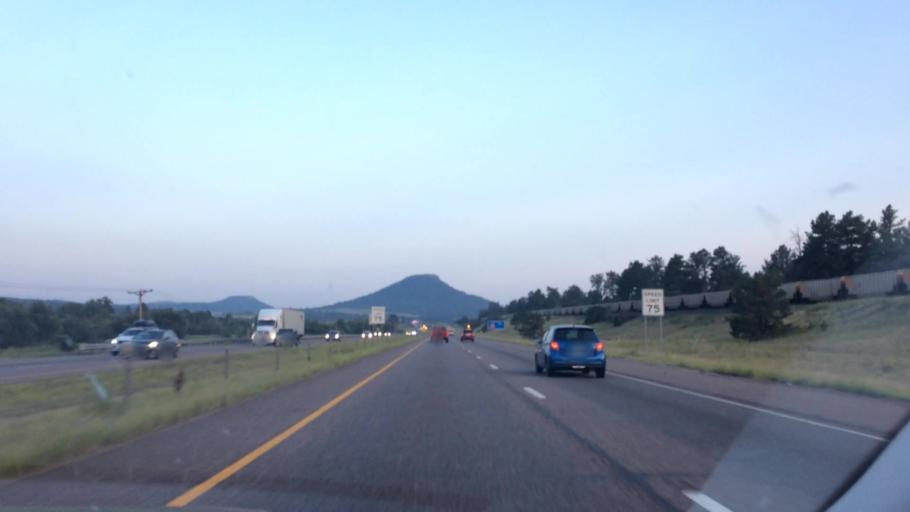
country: US
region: Colorado
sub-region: Douglas County
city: Perry Park
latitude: 39.2580
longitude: -104.8911
